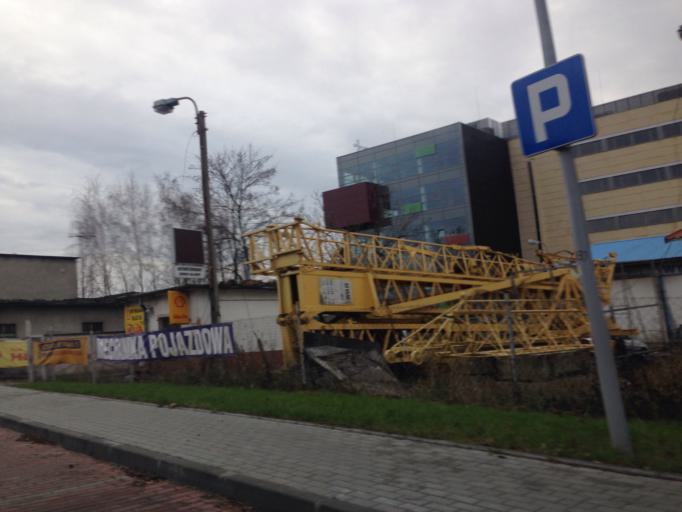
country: PL
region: Kujawsko-Pomorskie
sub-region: Torun
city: Torun
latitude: 53.0258
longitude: 18.6266
